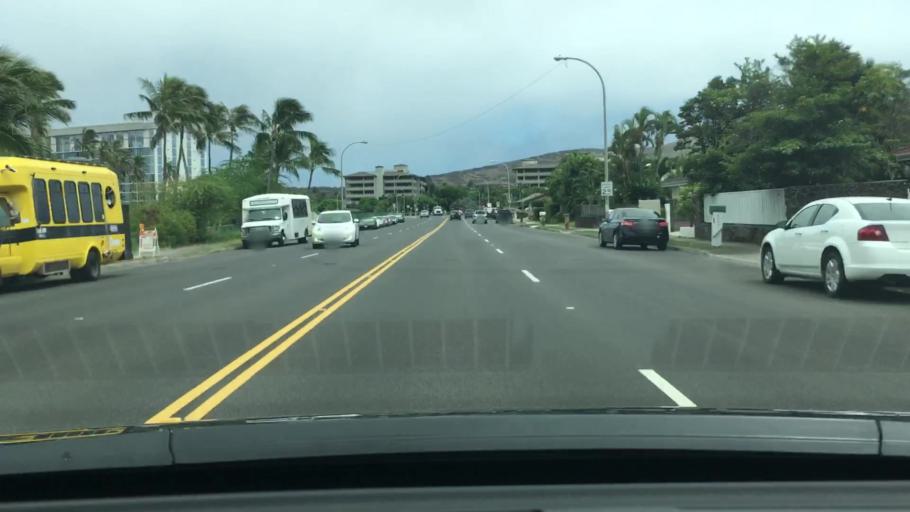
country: US
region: Hawaii
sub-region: Honolulu County
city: Waimanalo Beach
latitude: 21.2893
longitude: -157.7071
